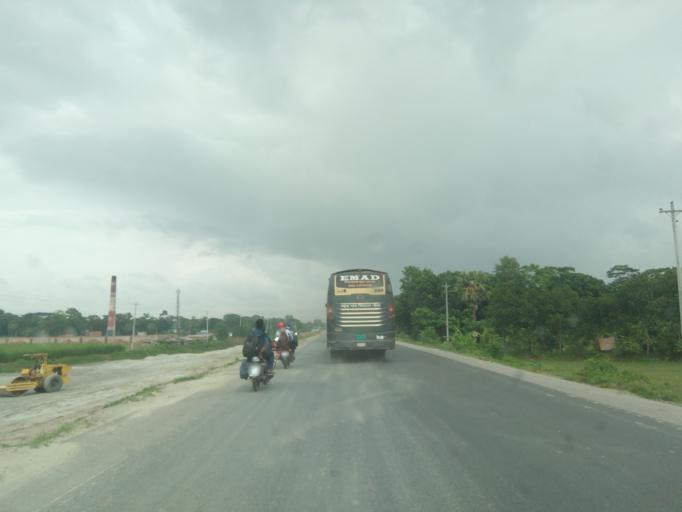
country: BD
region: Dhaka
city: Char Bhadrasan
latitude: 23.3695
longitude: 90.0633
